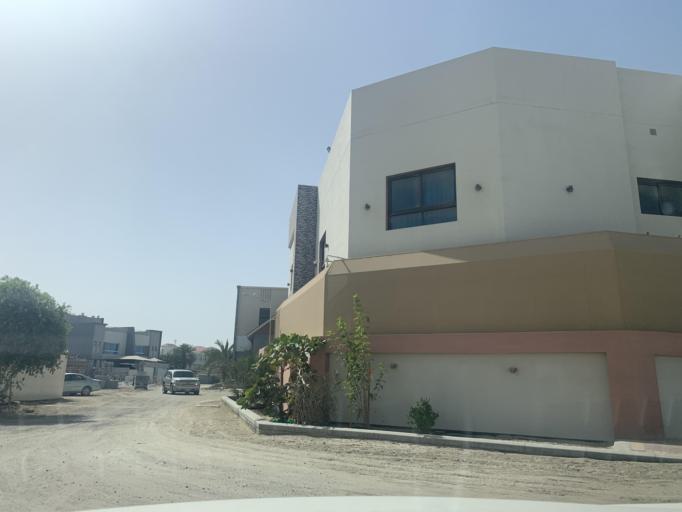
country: BH
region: Northern
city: Sitrah
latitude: 26.1715
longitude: 50.6260
